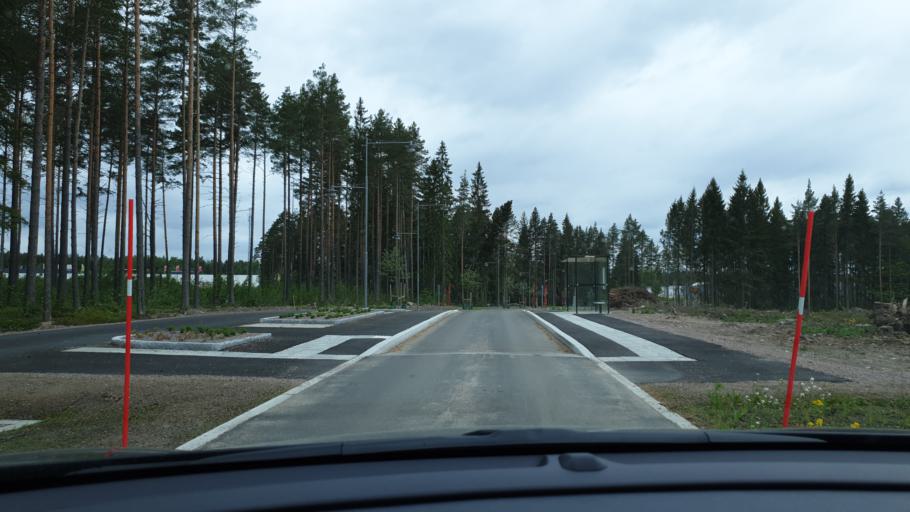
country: SE
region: Gaevleborg
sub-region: Gavle Kommun
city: Gavle
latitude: 60.6418
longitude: 17.1513
